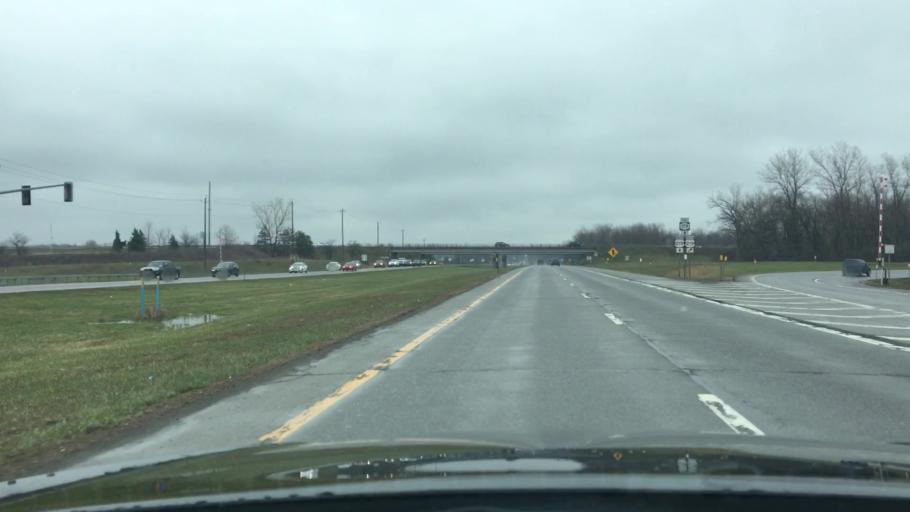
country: US
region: New York
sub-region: Erie County
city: Orchard Park
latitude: 42.7890
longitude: -78.7786
